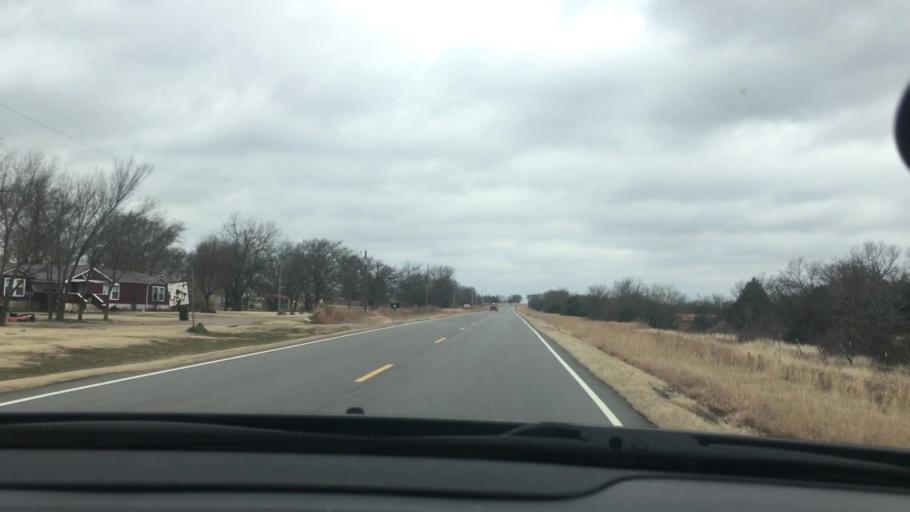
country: US
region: Oklahoma
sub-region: Atoka County
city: Atoka
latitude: 34.3747
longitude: -96.1846
